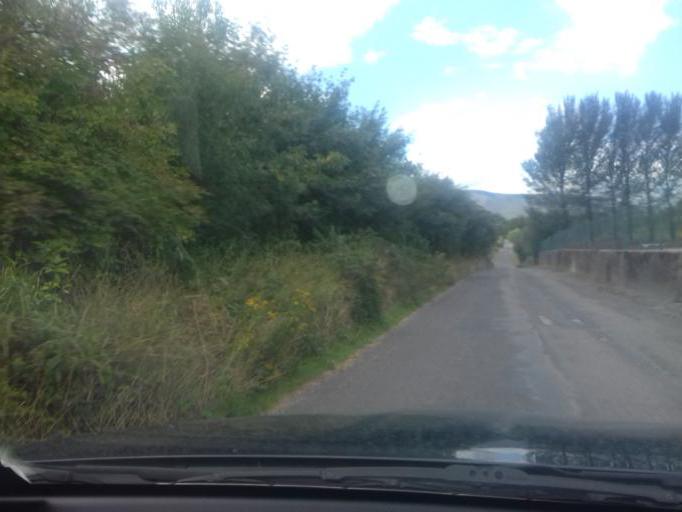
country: IE
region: Munster
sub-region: Waterford
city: Portlaw
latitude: 52.2113
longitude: -7.4275
